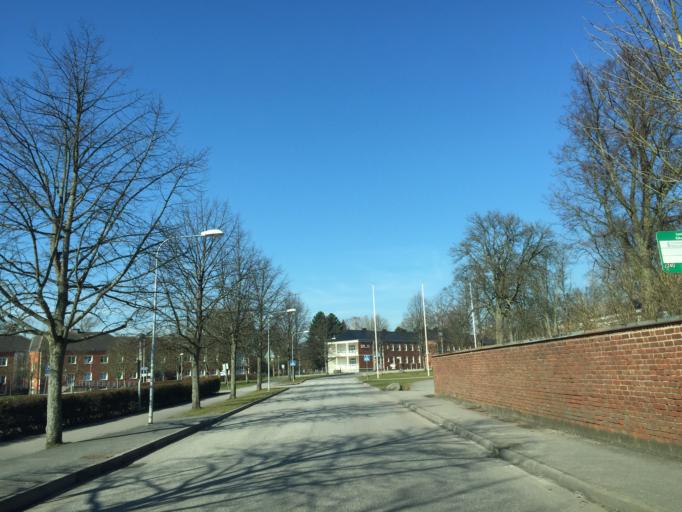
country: SE
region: Skane
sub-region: Lunds Kommun
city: Lund
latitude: 55.6854
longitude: 13.1811
